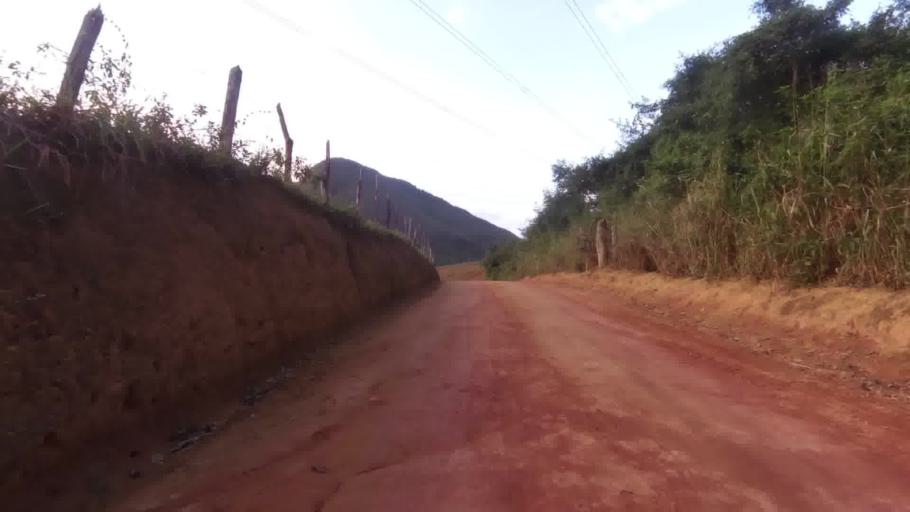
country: BR
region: Espirito Santo
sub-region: Guarapari
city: Guarapari
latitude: -20.6854
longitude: -40.6284
